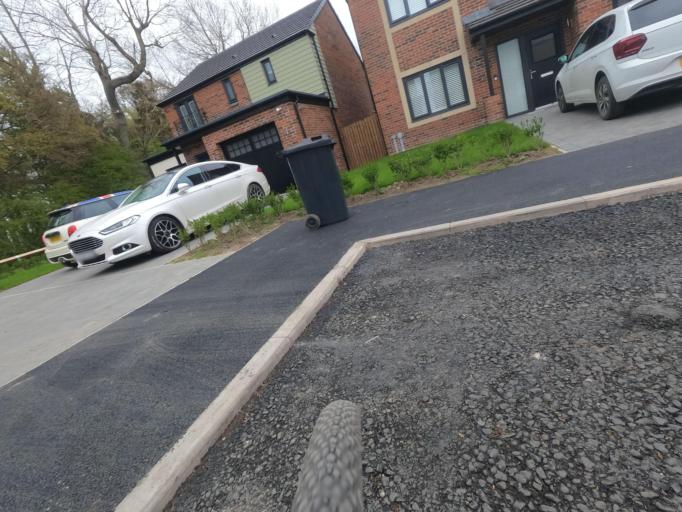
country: GB
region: England
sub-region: Northumberland
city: Ponteland
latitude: 55.0592
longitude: -1.7646
